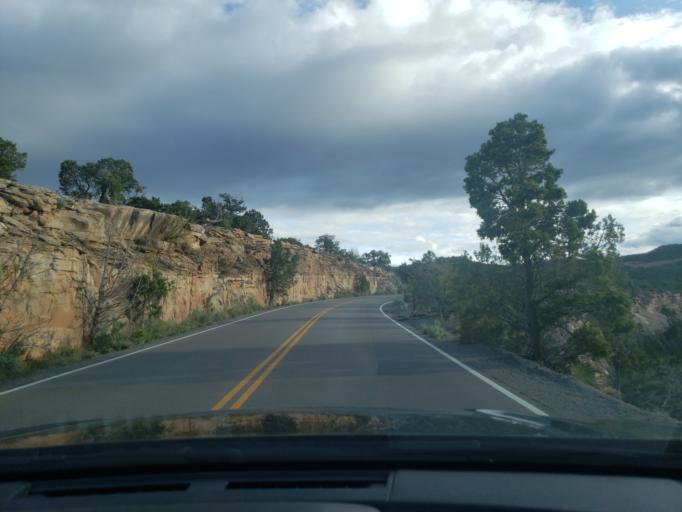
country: US
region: Colorado
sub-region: Mesa County
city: Redlands
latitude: 39.0284
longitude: -108.6561
